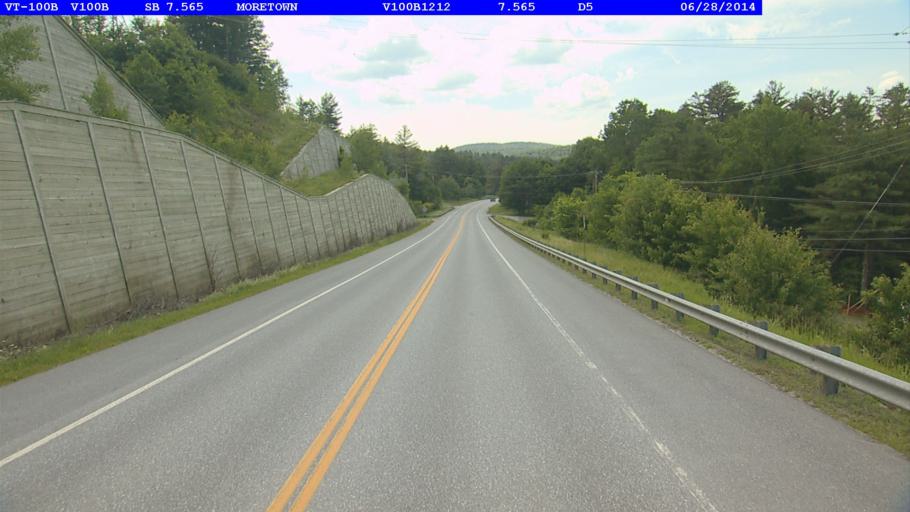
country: US
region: Vermont
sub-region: Washington County
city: Waterbury
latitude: 44.2918
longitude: -72.6841
